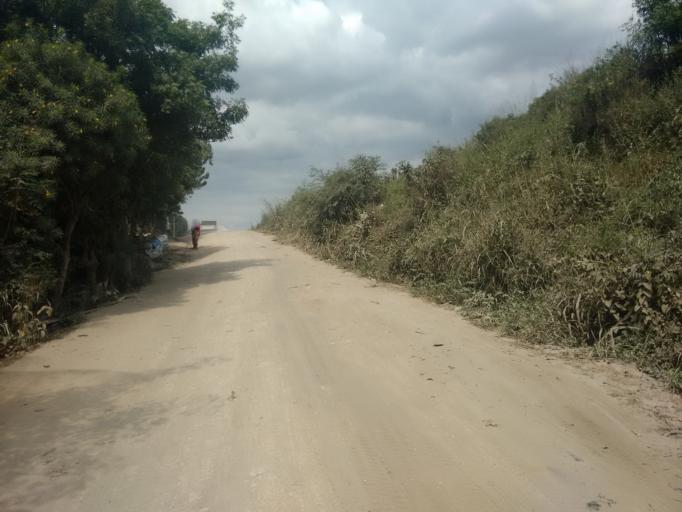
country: TZ
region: Dar es Salaam
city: Dar es Salaam
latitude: -6.8564
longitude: 39.2431
